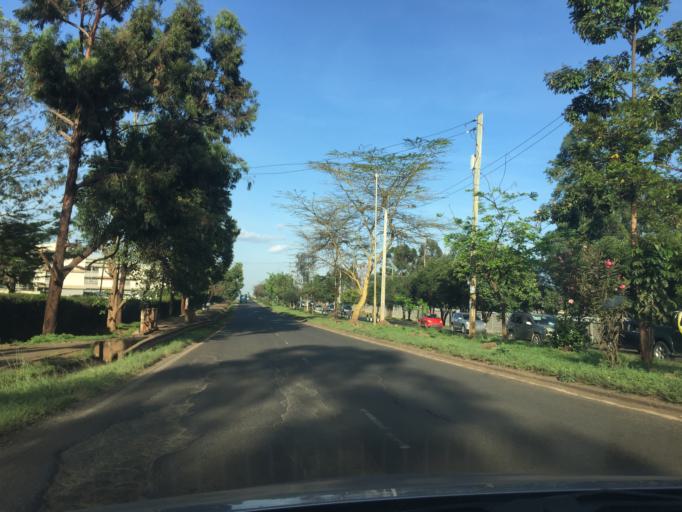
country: KE
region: Nairobi Area
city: Nairobi
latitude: -1.3310
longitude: 36.7848
